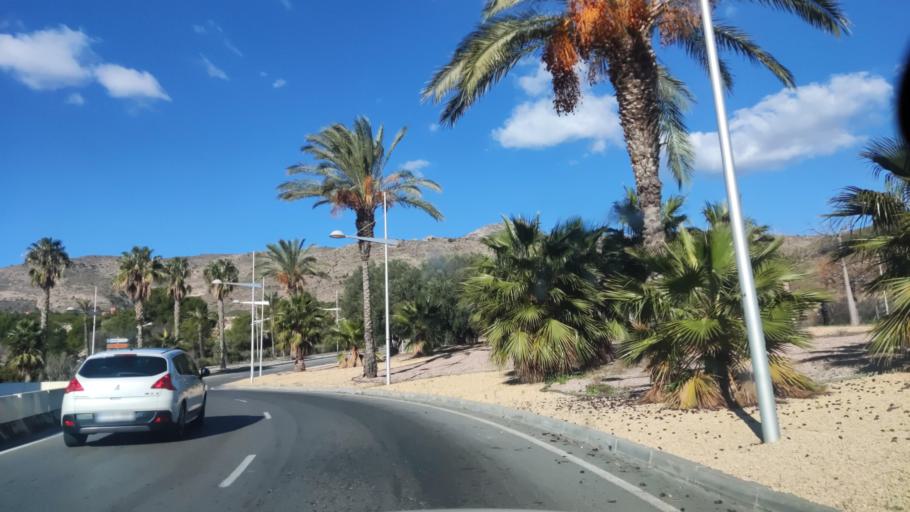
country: ES
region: Valencia
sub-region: Provincia de Alicante
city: Benidorm
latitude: 38.5499
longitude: -0.1627
